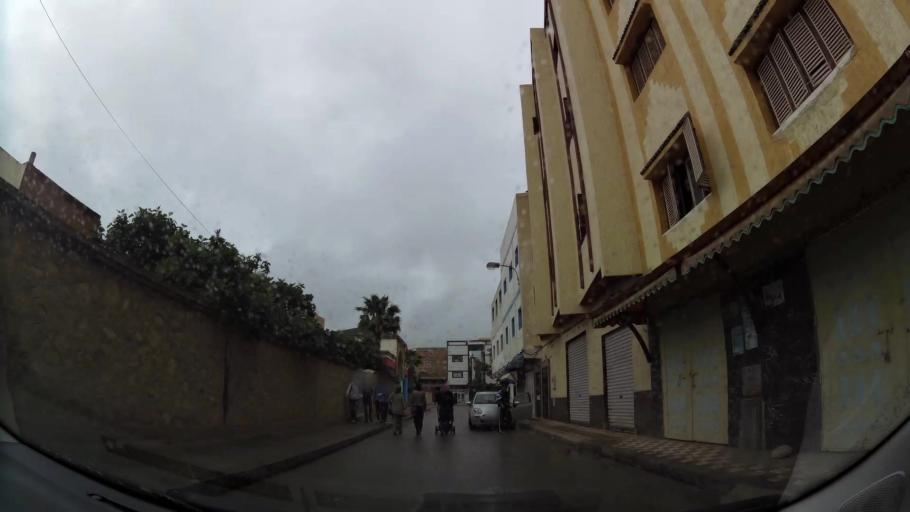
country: MA
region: Taza-Al Hoceima-Taounate
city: Imzourene
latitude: 35.1405
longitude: -3.8495
